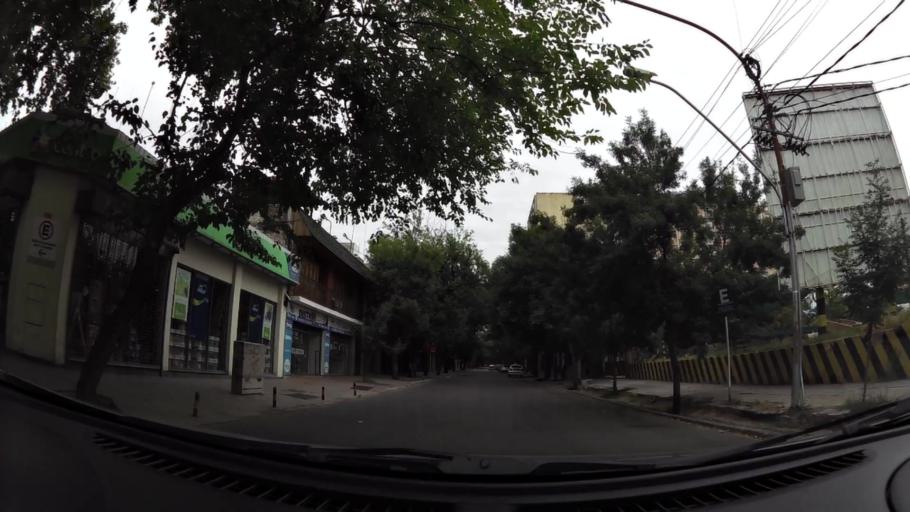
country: AR
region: Mendoza
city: Mendoza
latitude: -32.8877
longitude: -68.8328
